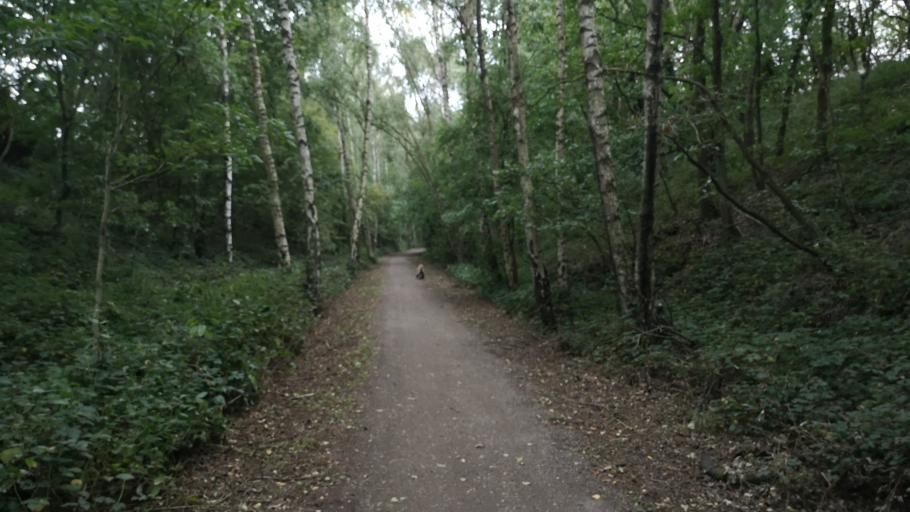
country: GB
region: England
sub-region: Barnsley
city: Royston
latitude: 53.6171
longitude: -1.4520
